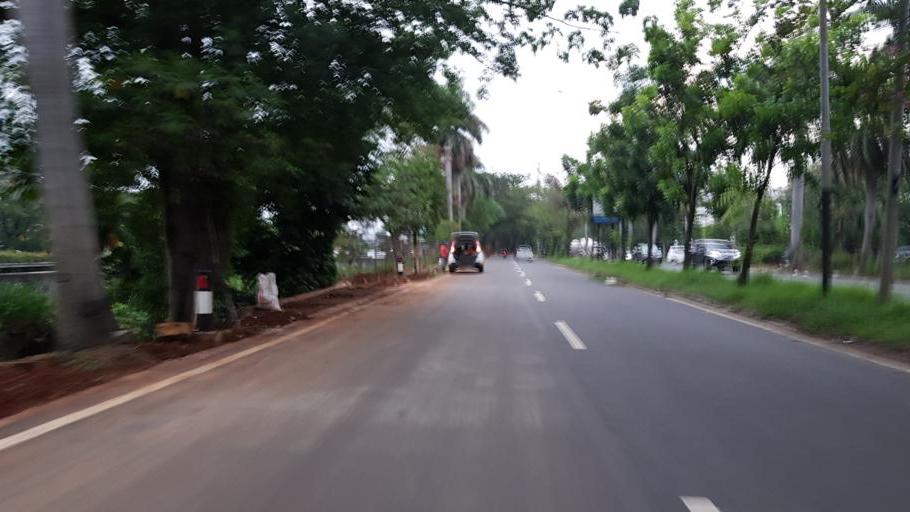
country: ID
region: West Java
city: Ciputat
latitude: -6.1912
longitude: 106.7375
